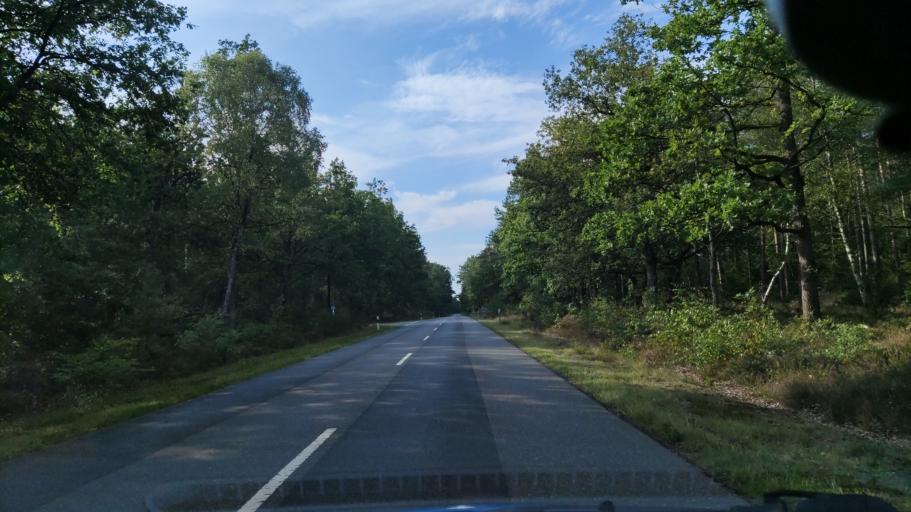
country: DE
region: Lower Saxony
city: Fassberg
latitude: 52.9661
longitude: 10.1700
